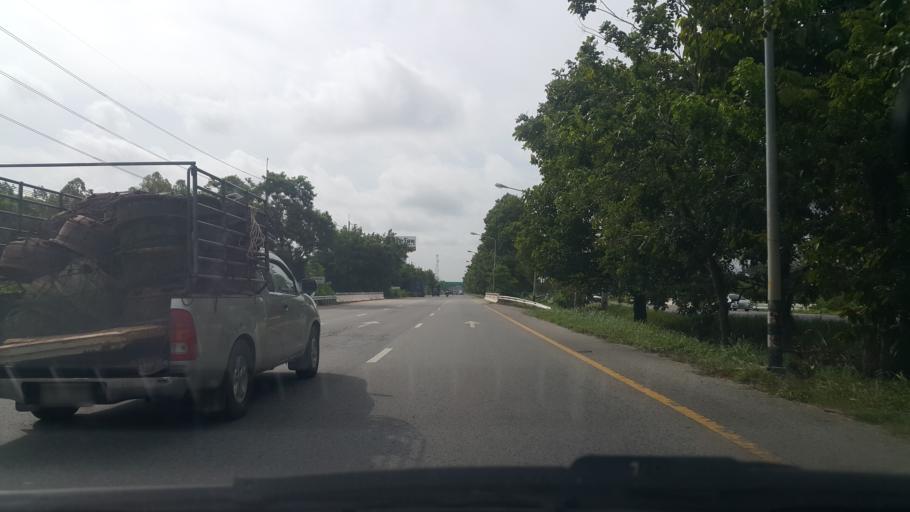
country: TH
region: Rayong
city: Rayong
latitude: 12.6669
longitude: 101.3075
